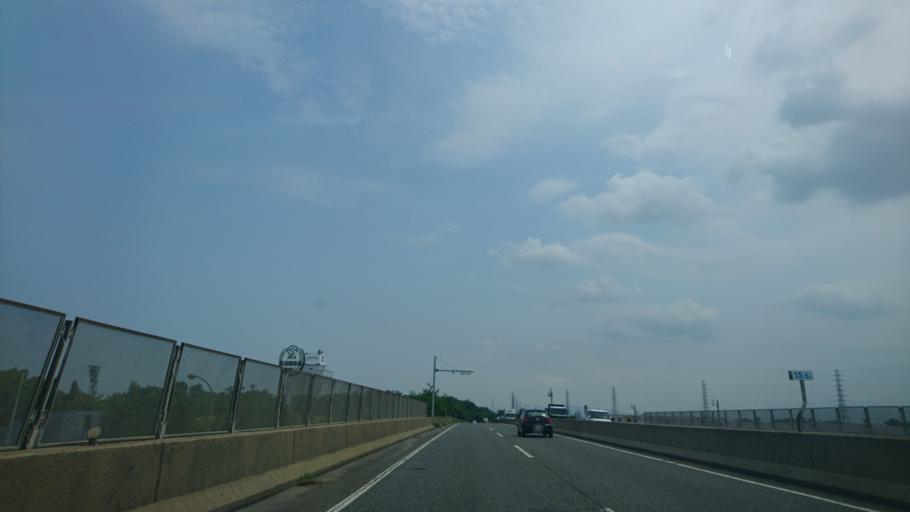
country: JP
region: Niigata
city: Kameda-honcho
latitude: 37.9423
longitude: 139.1833
